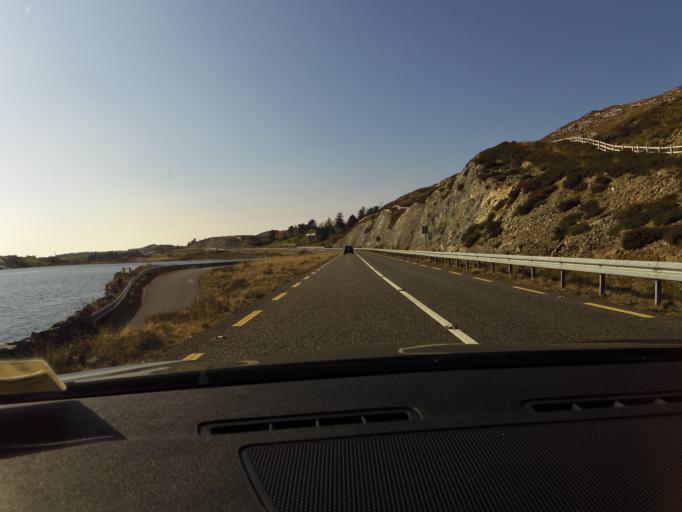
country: IE
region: Connaught
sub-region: County Galway
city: Clifden
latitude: 53.4819
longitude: -9.9438
